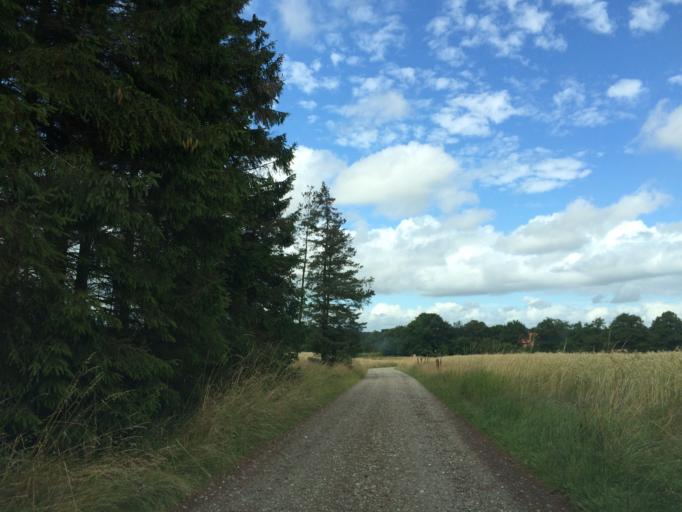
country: DK
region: Central Jutland
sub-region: Silkeborg Kommune
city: Svejbaek
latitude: 56.2043
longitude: 9.6728
